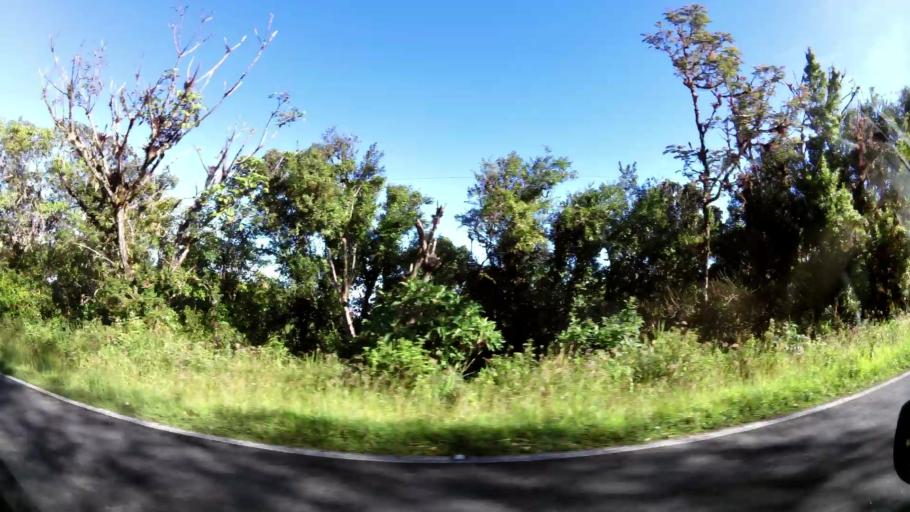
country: CR
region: San Jose
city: San Marcos
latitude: 9.6976
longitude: -83.9309
